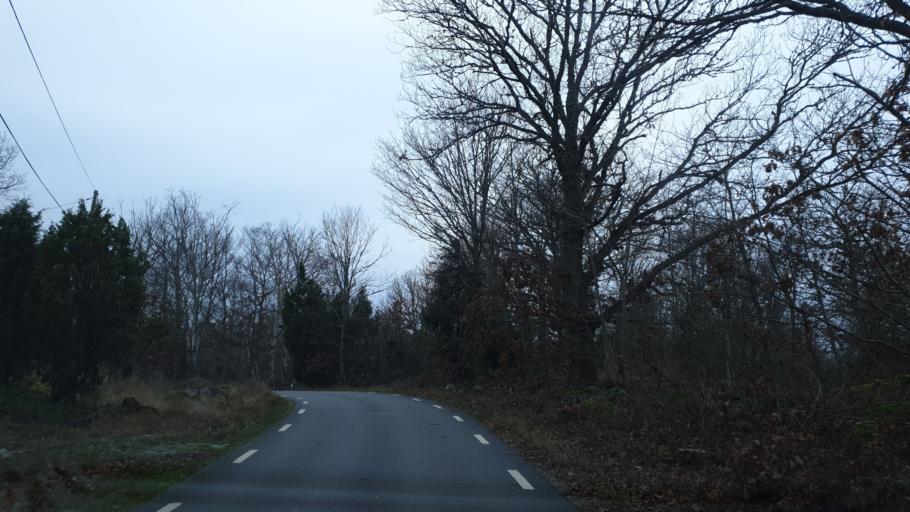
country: SE
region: Blekinge
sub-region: Karlskrona Kommun
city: Karlskrona
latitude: 56.1283
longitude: 15.6263
